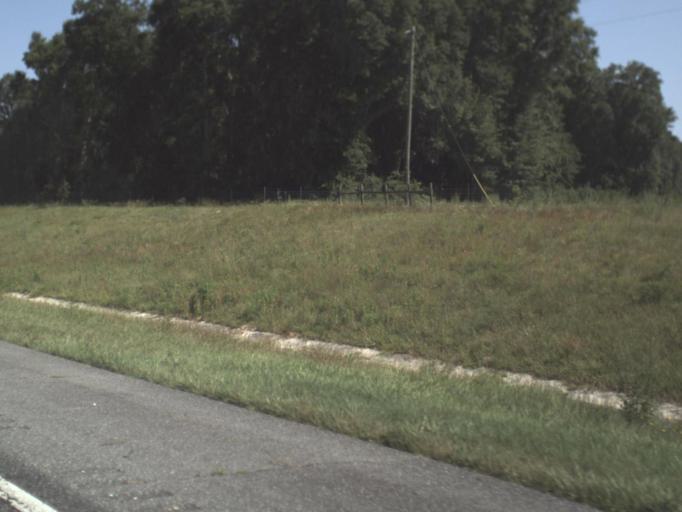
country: US
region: Florida
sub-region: Suwannee County
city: Live Oak
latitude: 30.3159
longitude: -82.9411
